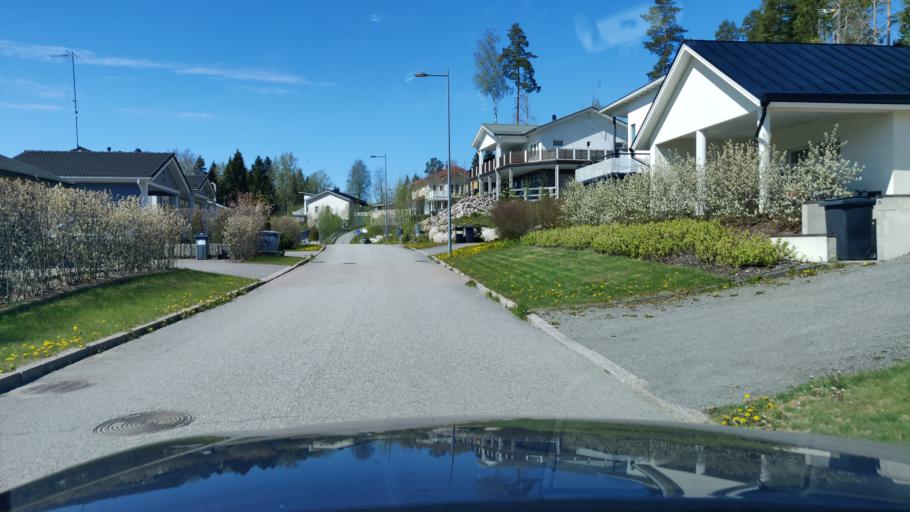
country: FI
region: Uusimaa
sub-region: Helsinki
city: Nurmijaervi
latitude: 60.3615
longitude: 24.7520
